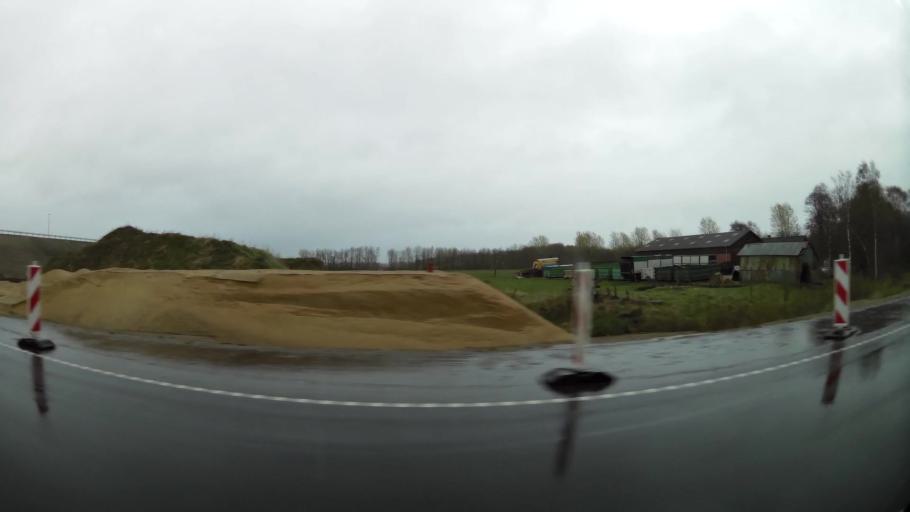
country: DK
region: Central Jutland
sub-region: Herning Kommune
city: Avlum
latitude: 56.2185
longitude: 8.8512
